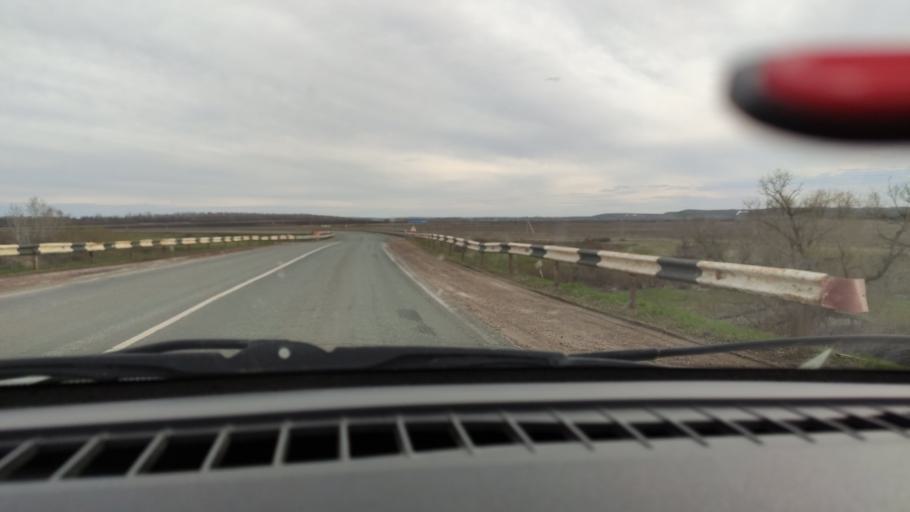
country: RU
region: Bashkortostan
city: Yermolayevo
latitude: 52.4743
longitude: 55.8291
